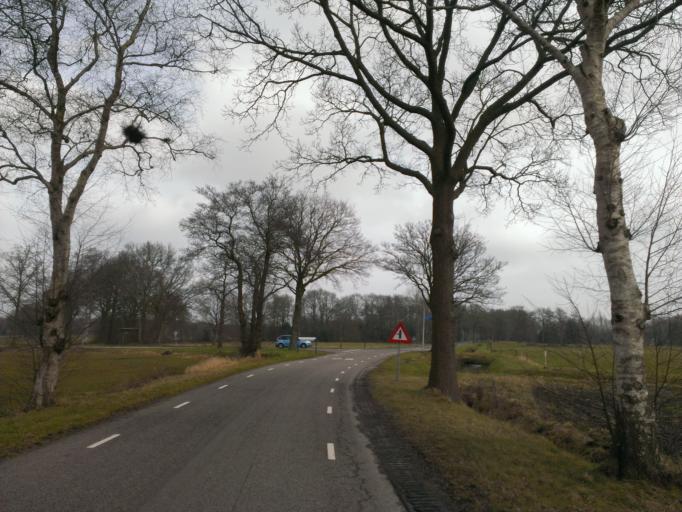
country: NL
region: Drenthe
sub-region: Gemeente Hoogeveen
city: Hoogeveen
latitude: 52.7319
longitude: 6.4331
